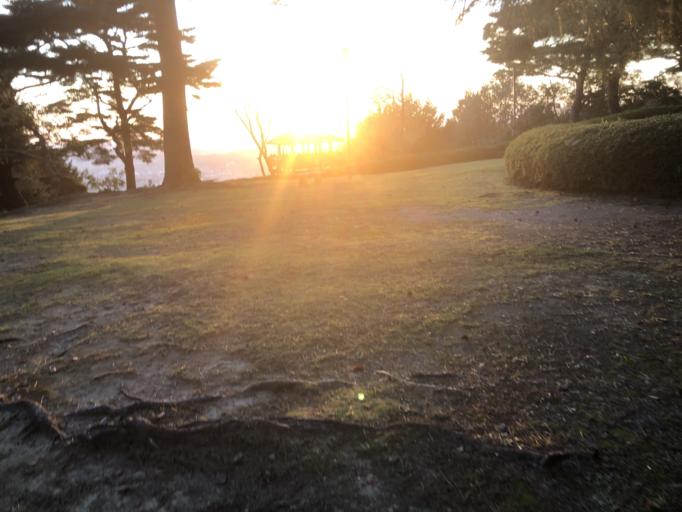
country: JP
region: Shizuoka
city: Mori
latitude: 34.8476
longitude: 137.9500
